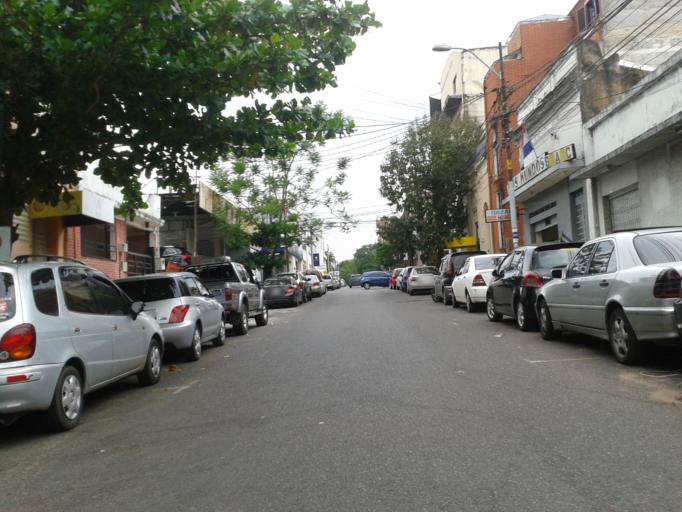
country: PY
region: Asuncion
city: Asuncion
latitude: -25.2863
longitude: -57.6351
